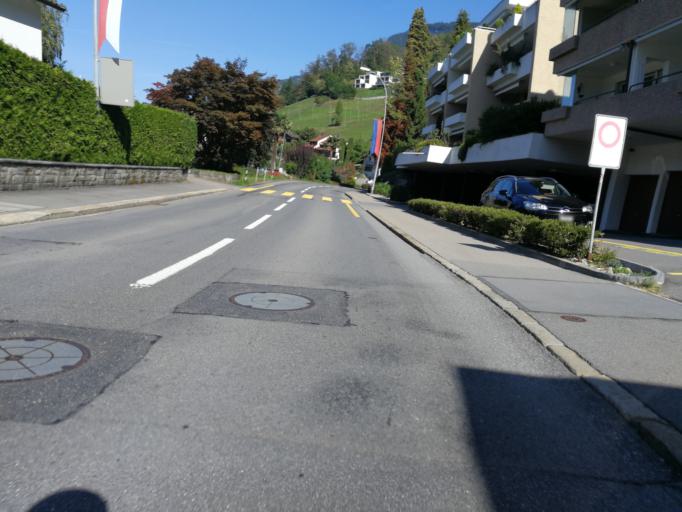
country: CH
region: Lucerne
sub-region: Lucerne-Land District
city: Vitznau
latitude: 47.0129
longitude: 8.4825
